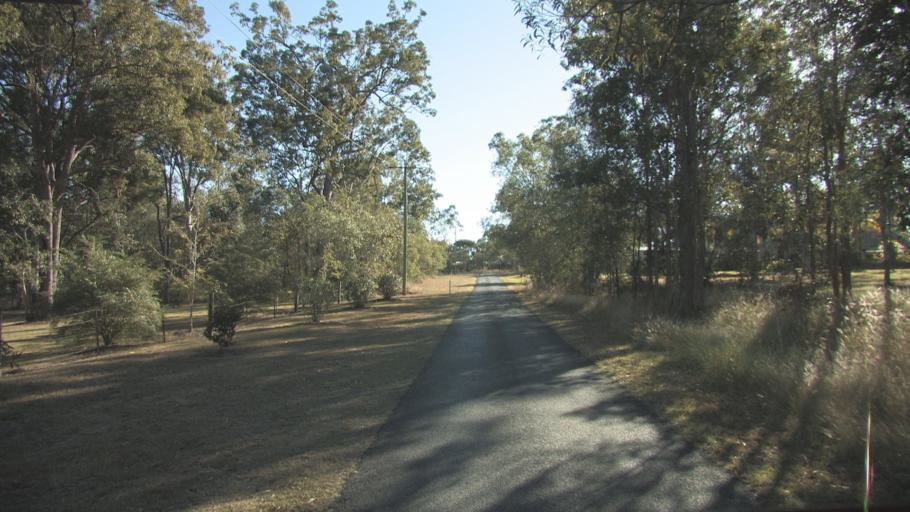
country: AU
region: Queensland
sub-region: Logan
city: North Maclean
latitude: -27.7882
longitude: 152.9609
